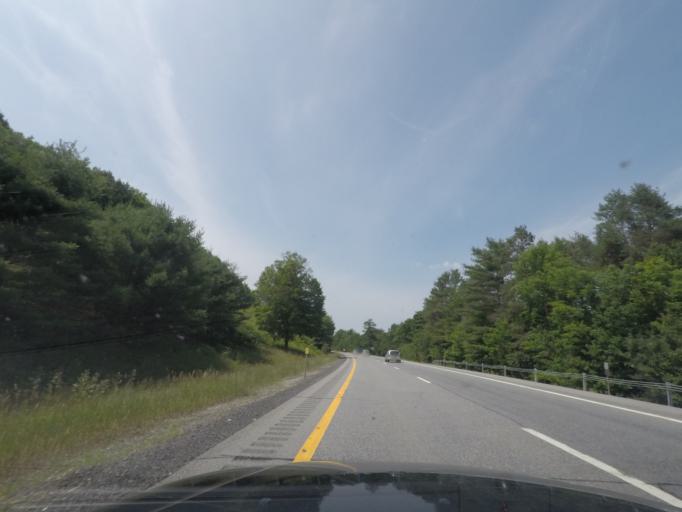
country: US
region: New York
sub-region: Warren County
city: Warrensburg
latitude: 43.6569
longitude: -73.7659
